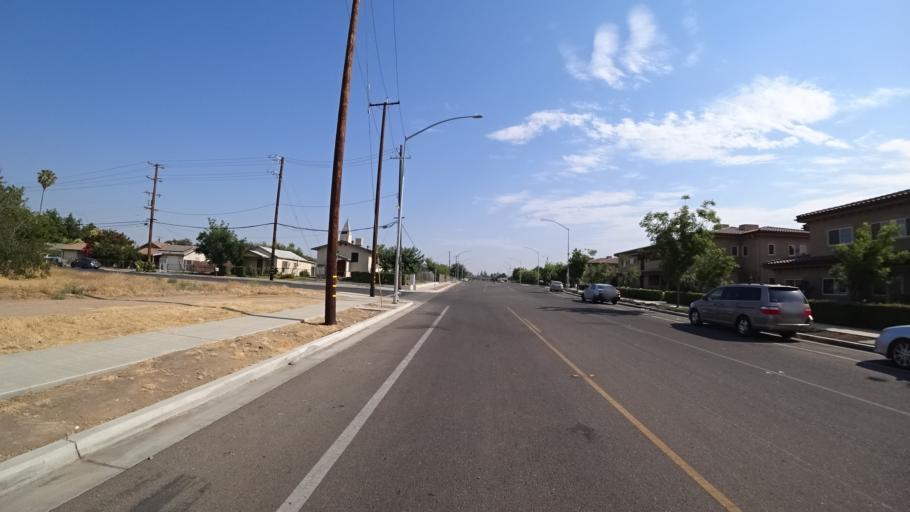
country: US
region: California
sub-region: Fresno County
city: West Park
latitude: 36.7184
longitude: -119.8112
